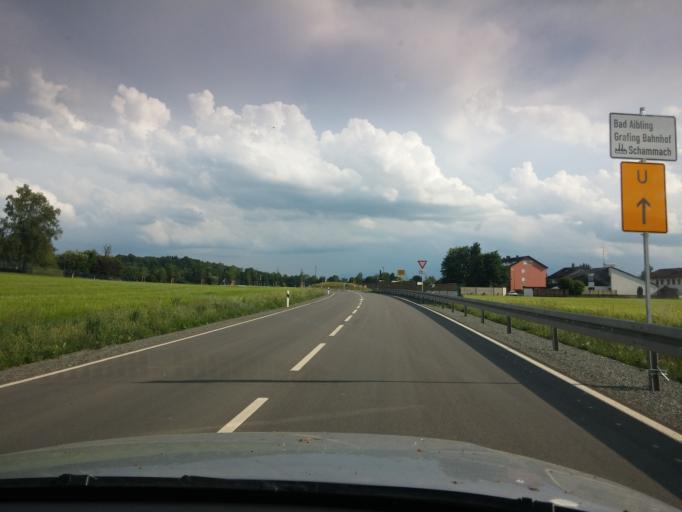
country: DE
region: Bavaria
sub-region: Upper Bavaria
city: Grafing bei Munchen
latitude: 48.0483
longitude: 11.9749
